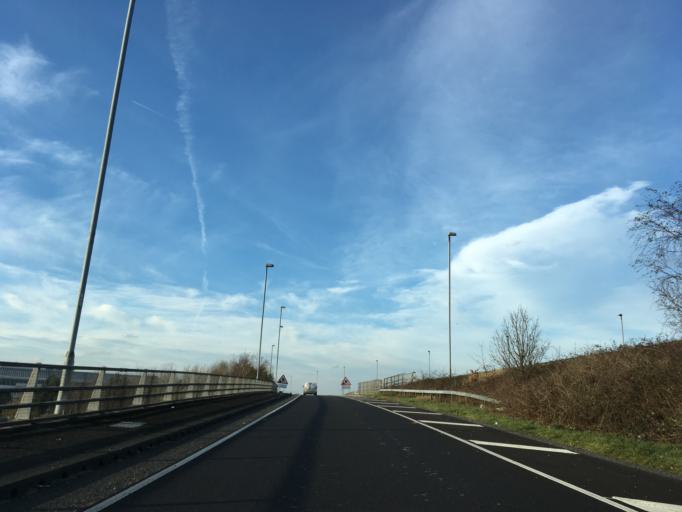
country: GB
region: England
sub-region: Borough of Stockport
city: Cheadle Hulme
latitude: 53.3562
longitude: -2.2021
